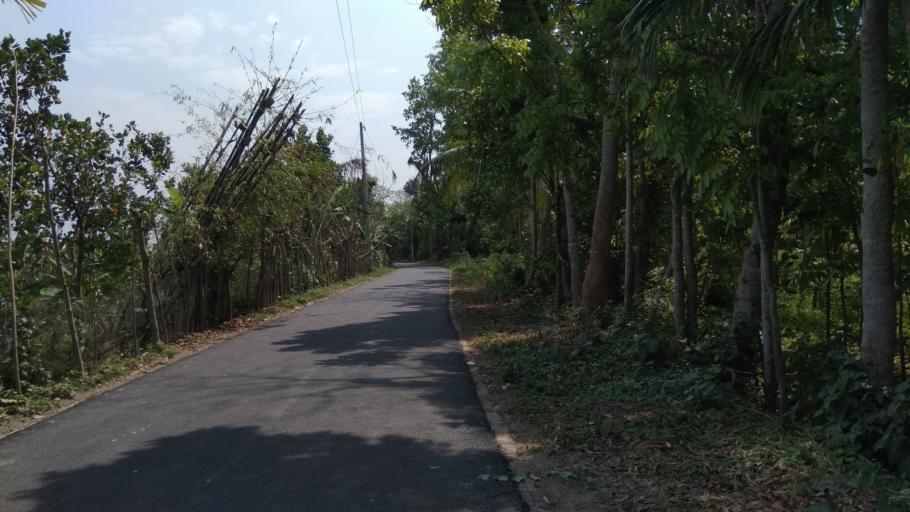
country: BD
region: Barisal
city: Mehendiganj
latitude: 22.9274
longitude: 90.3911
